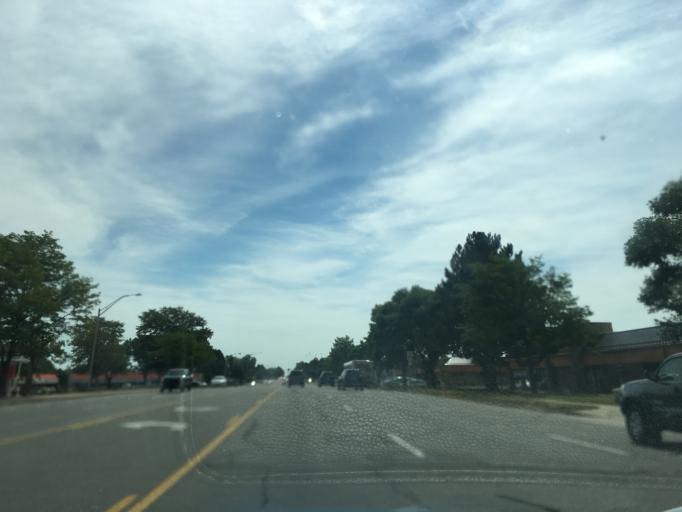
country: US
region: Colorado
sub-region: Adams County
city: Aurora
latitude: 39.6747
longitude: -104.8696
